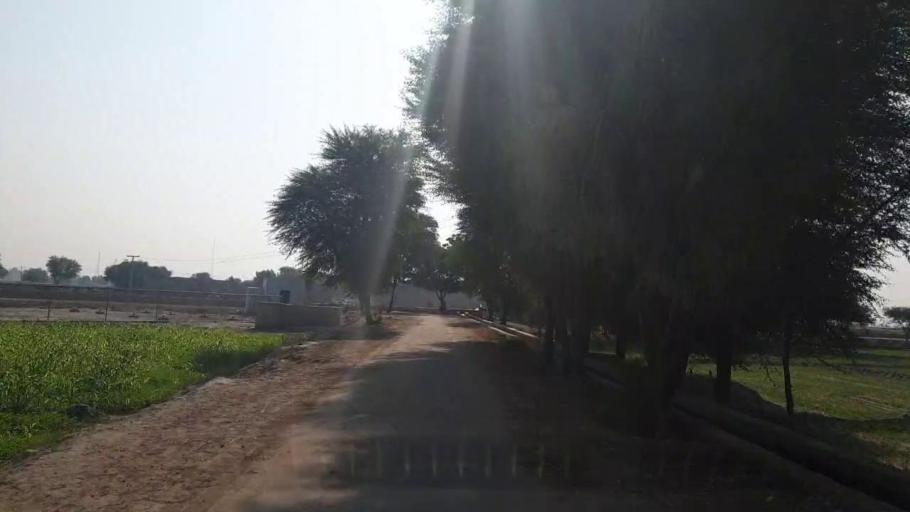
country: PK
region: Sindh
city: Sehwan
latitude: 26.4382
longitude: 67.8412
